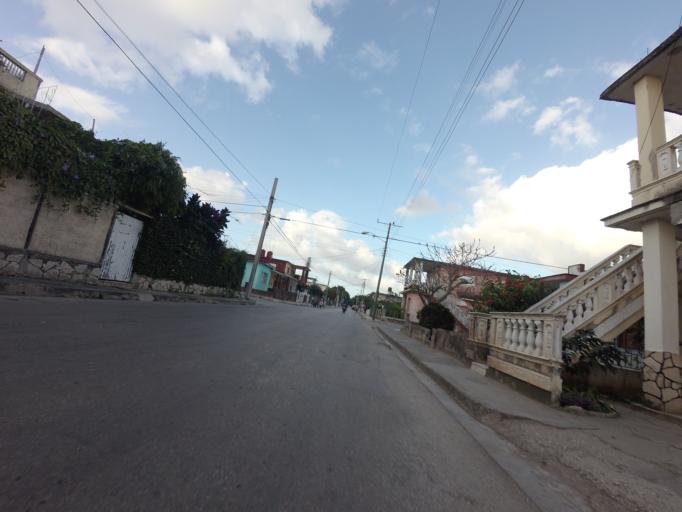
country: CU
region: Ciego de Avila
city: Ciego de Avila
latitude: 21.8367
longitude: -78.7559
